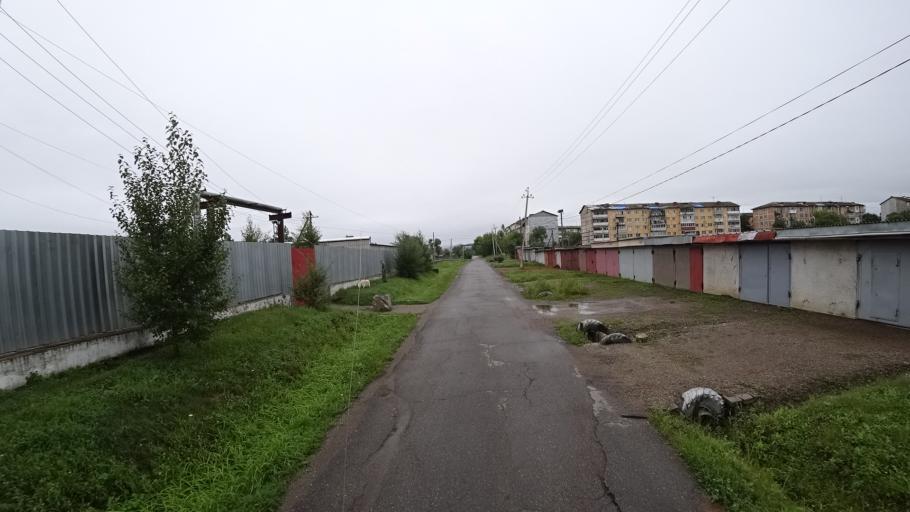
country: RU
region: Primorskiy
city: Monastyrishche
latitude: 44.2085
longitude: 132.4469
